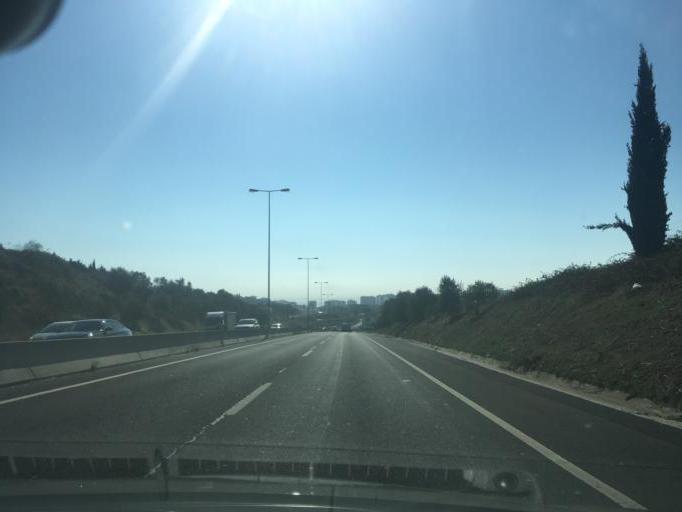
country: PT
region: Lisbon
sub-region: Oeiras
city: Porto Salvo
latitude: 38.7189
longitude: -9.2963
